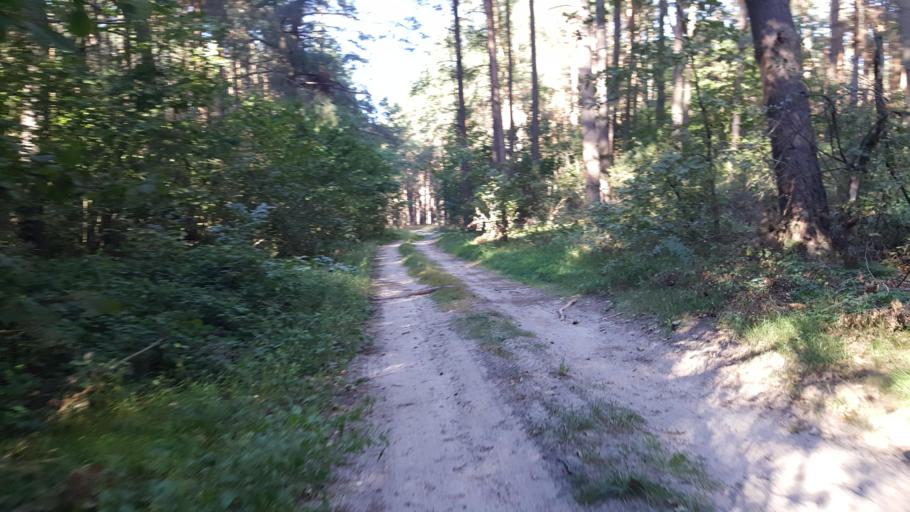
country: PL
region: Lublin Voivodeship
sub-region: Powiat bialski
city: Janow Podlaski
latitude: 52.3103
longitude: 23.2591
